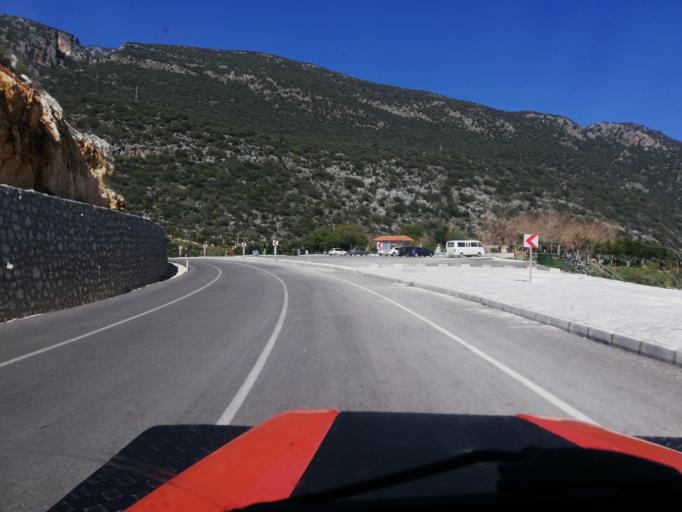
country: TR
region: Antalya
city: Kas
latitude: 36.2050
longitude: 29.6000
